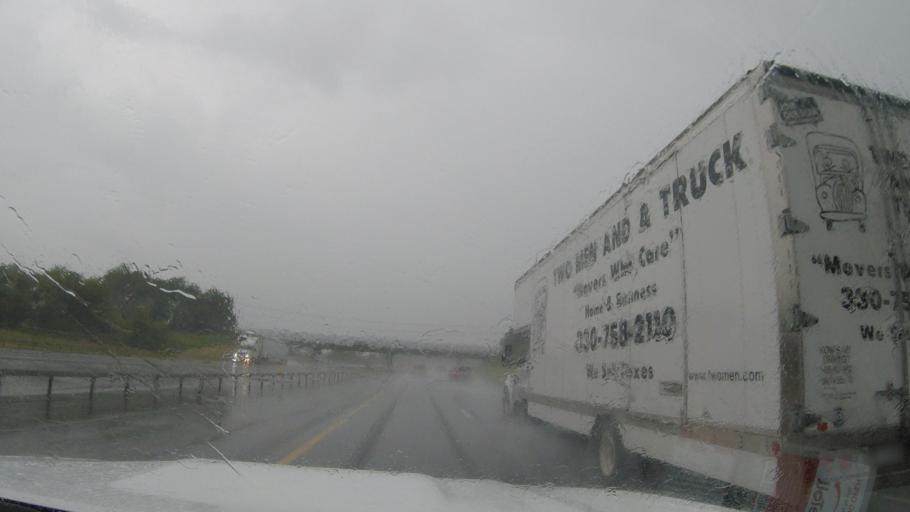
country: US
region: New York
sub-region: Ontario County
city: Phelps
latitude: 42.9683
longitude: -77.0591
